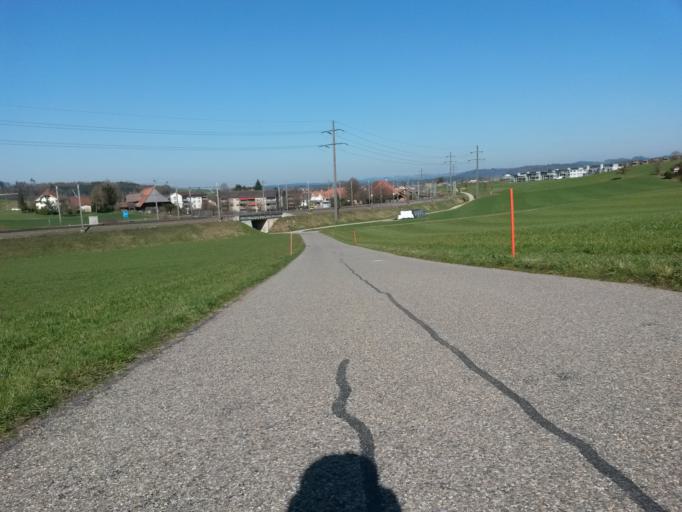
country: CH
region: Bern
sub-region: Bern-Mittelland District
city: Zollikofen
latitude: 47.0115
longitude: 7.4734
